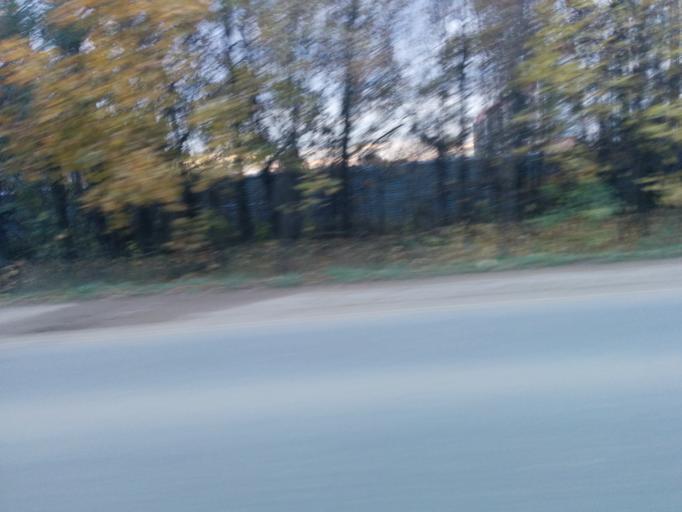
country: RU
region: Moscow
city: Zagor'ye
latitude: 55.5334
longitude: 37.6492
